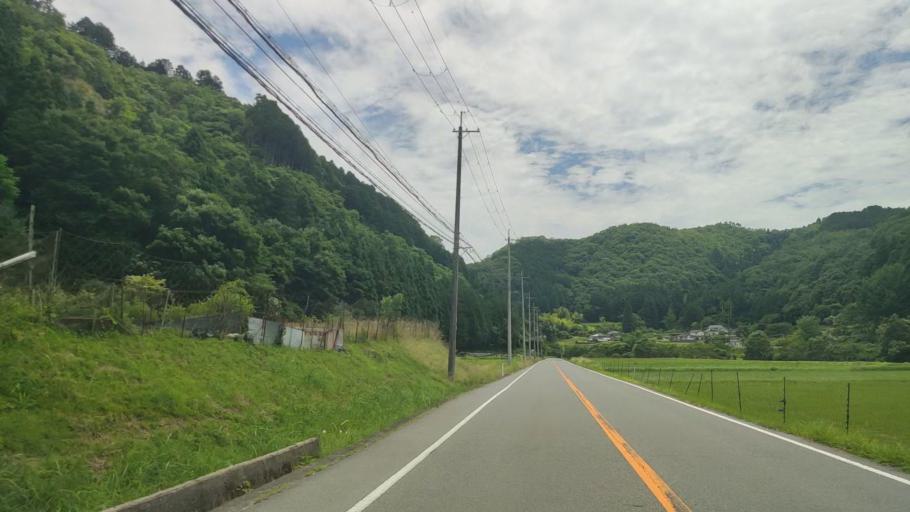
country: JP
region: Hyogo
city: Yamazakicho-nakabirose
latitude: 35.0858
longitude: 134.3590
